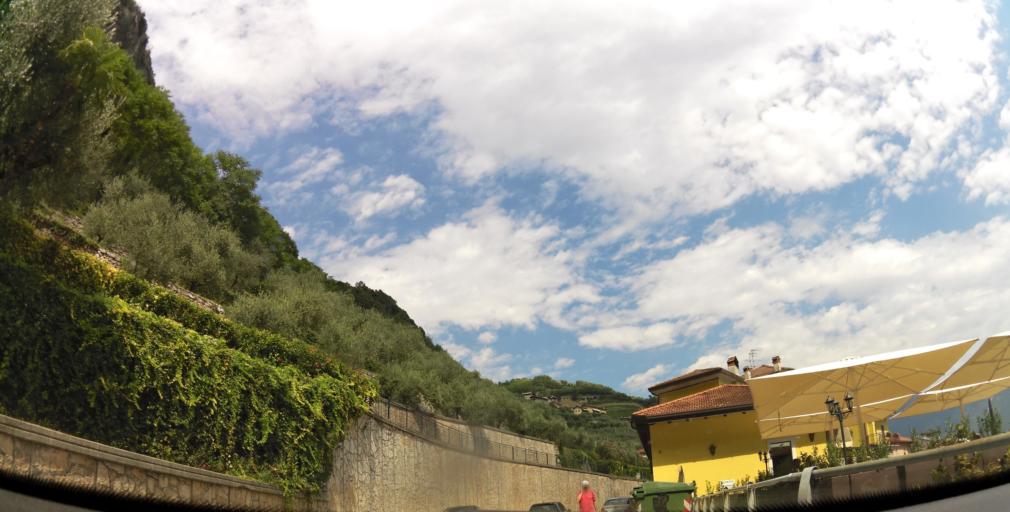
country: IT
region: Trentino-Alto Adige
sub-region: Provincia di Trento
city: Tenno
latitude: 45.9118
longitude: 10.8358
